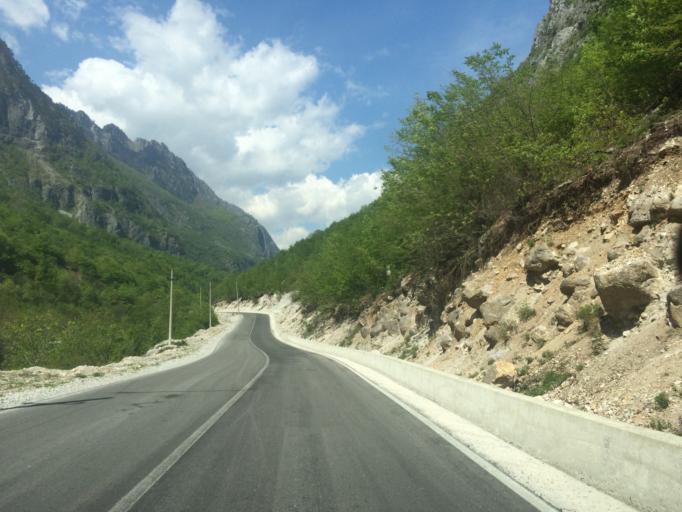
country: AL
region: Kukes
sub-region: Rrethi i Tropojes
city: Bajram Curri
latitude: 42.3958
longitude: 20.0521
